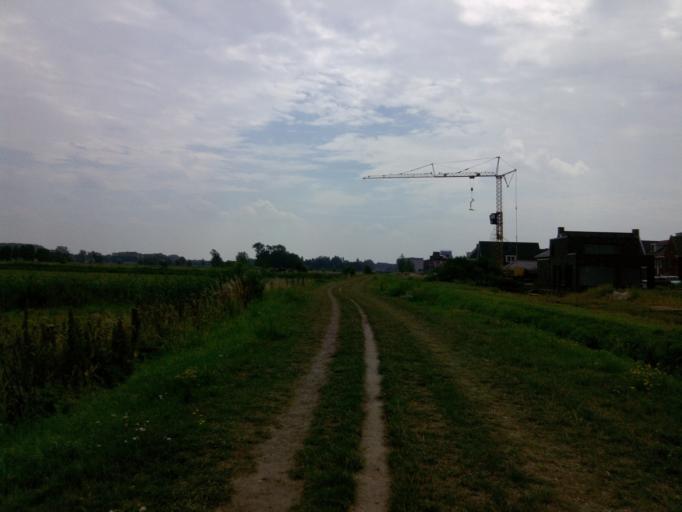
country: NL
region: Utrecht
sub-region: Gemeente Amersfoort
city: Hoogland
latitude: 52.2072
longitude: 5.4199
